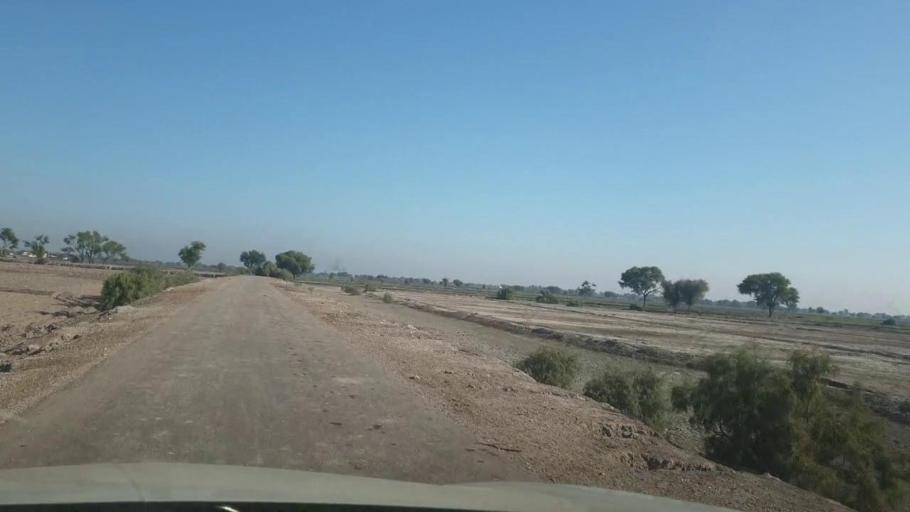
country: PK
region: Sindh
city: Bhan
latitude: 26.5277
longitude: 67.6743
